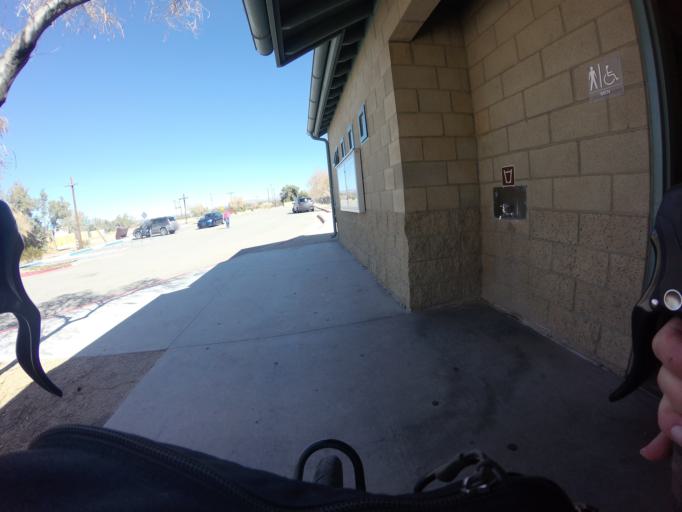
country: US
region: Nevada
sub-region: Clark County
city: Sandy Valley
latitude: 35.0124
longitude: -115.6524
